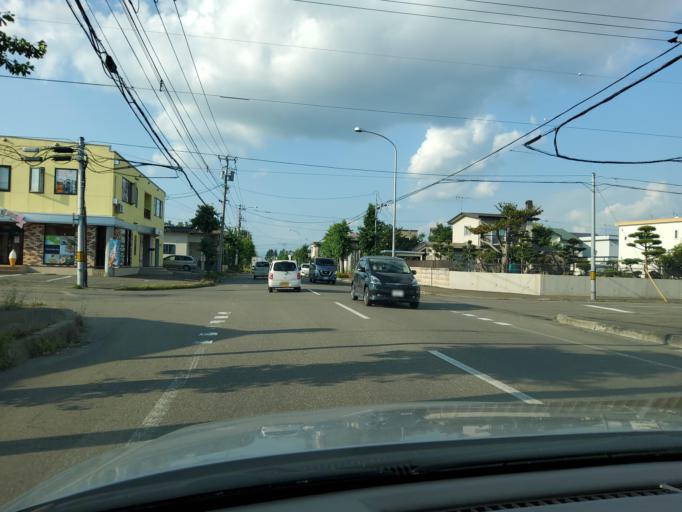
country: JP
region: Hokkaido
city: Obihiro
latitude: 42.9070
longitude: 143.1732
